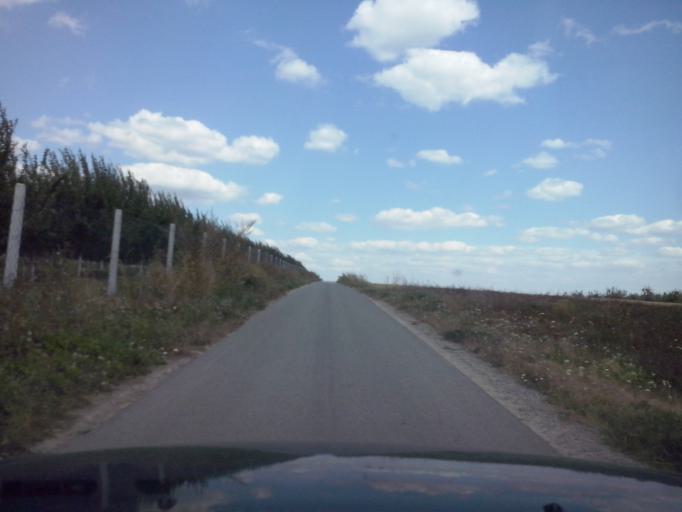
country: PL
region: Swietokrzyskie
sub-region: Powiat staszowski
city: Szydlow
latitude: 50.5919
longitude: 21.0707
